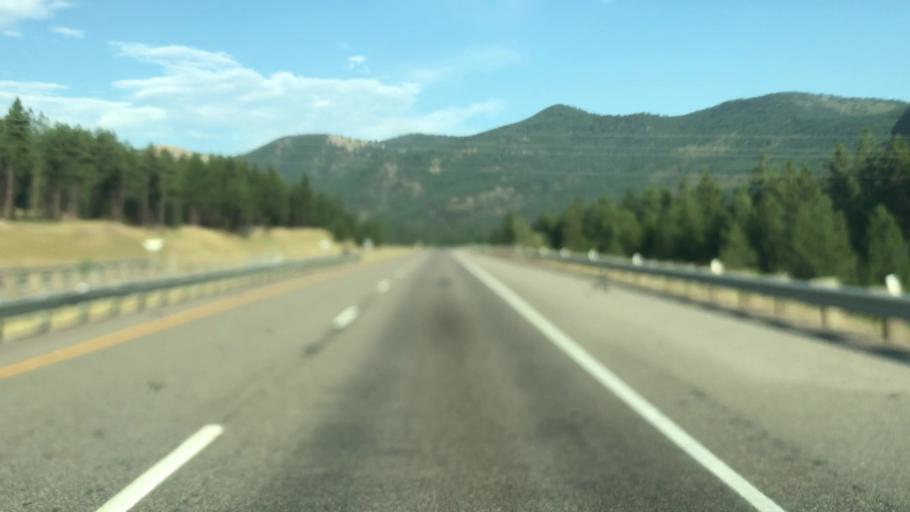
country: US
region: Montana
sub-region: Missoula County
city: Frenchtown
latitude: 46.9932
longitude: -114.4451
